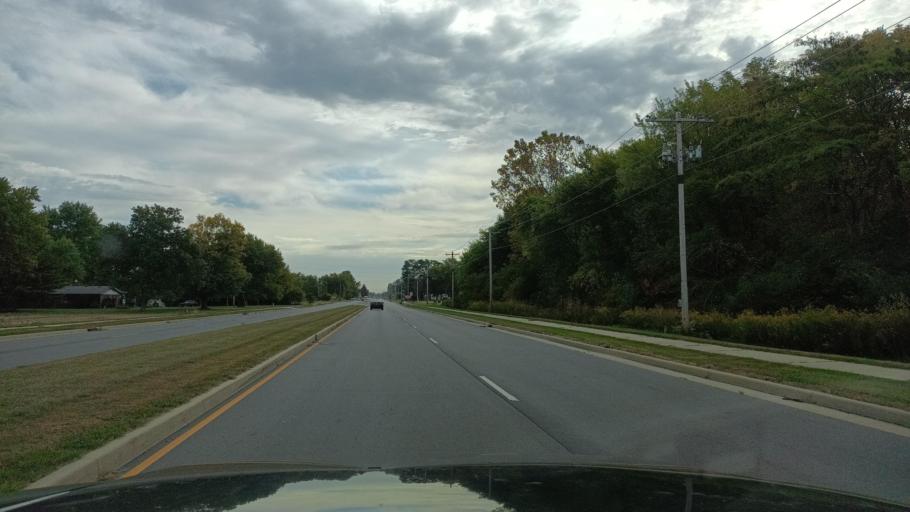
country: US
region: Indiana
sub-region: Delaware County
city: Yorktown
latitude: 40.1812
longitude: -85.4706
